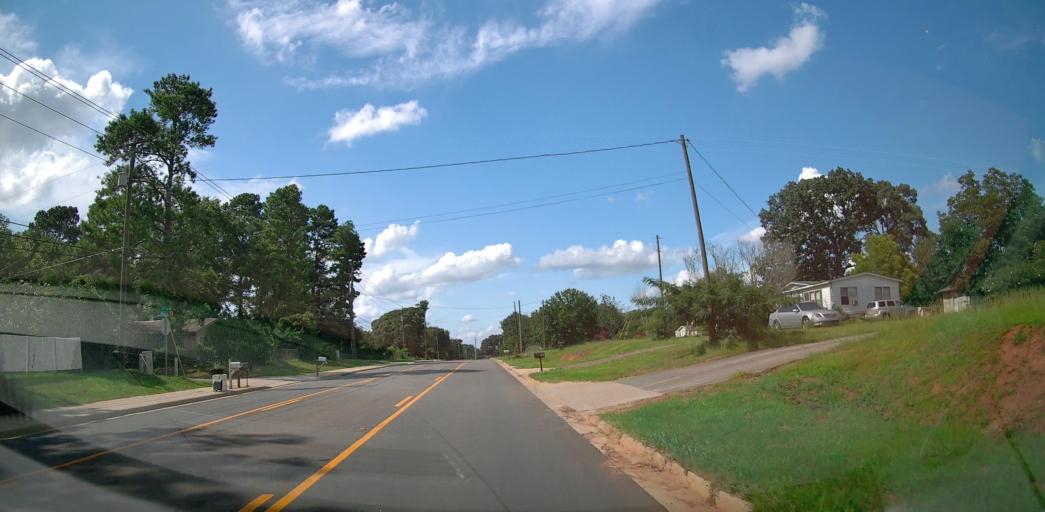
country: US
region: Georgia
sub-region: Houston County
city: Perry
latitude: 32.5239
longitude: -83.6911
